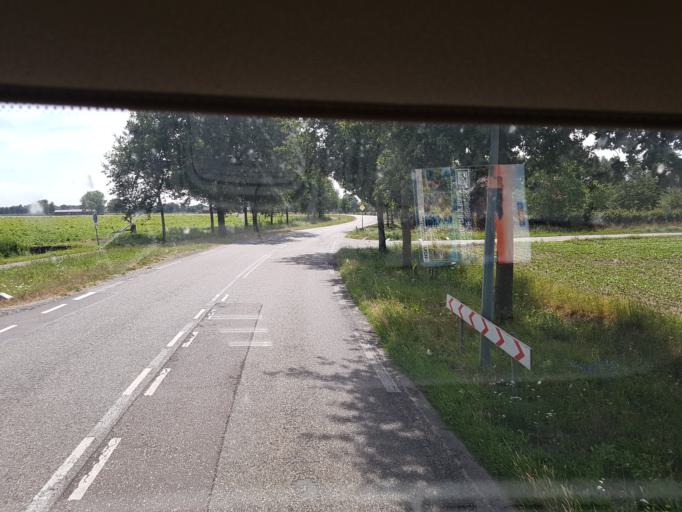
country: NL
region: Limburg
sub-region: Gemeente Leudal
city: Kelpen-Oler
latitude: 51.1853
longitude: 5.8176
